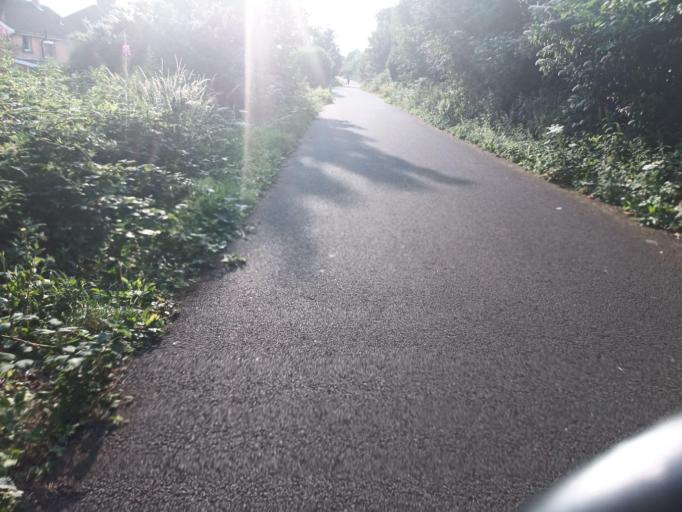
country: GB
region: Northern Ireland
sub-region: Castlereagh District
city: Dundonald
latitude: 54.5910
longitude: -5.8409
